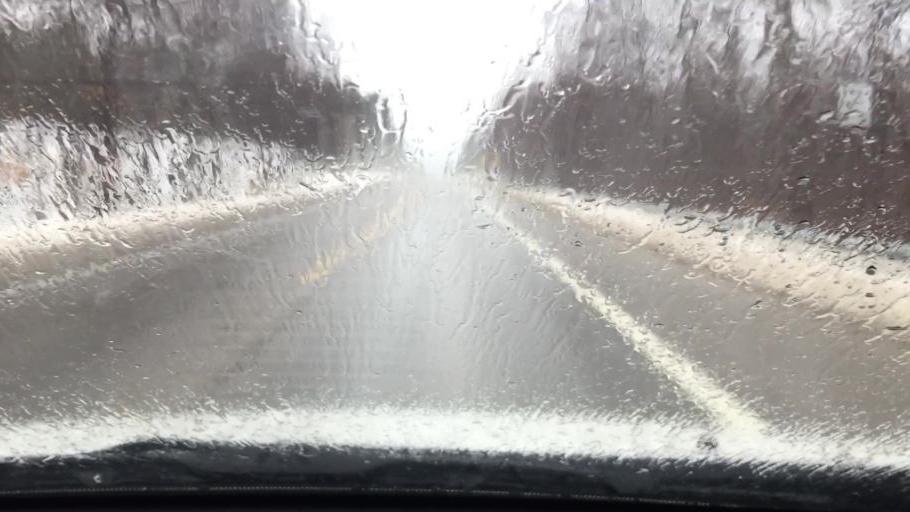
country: US
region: Michigan
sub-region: Charlevoix County
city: Charlevoix
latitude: 45.2635
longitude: -85.1972
